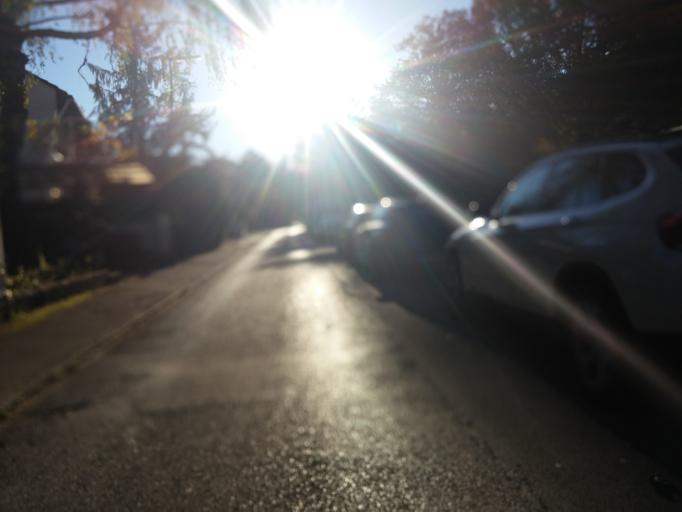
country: DE
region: Bavaria
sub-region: Upper Bavaria
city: Haar
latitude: 48.1115
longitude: 11.7020
